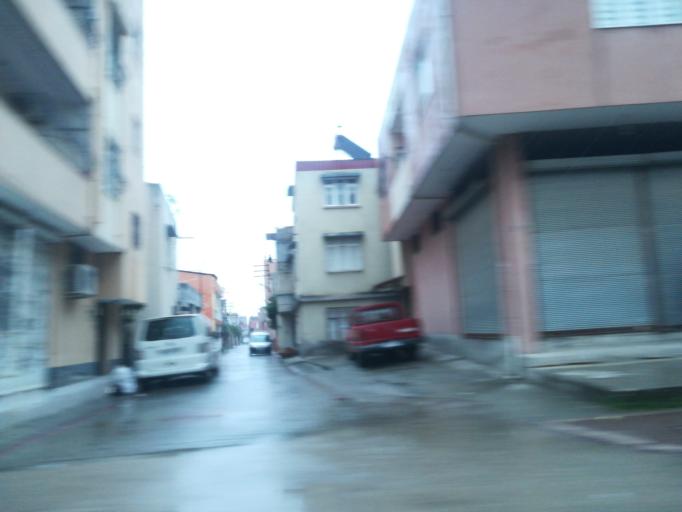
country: TR
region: Adana
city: Seyhan
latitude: 36.9998
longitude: 35.2799
